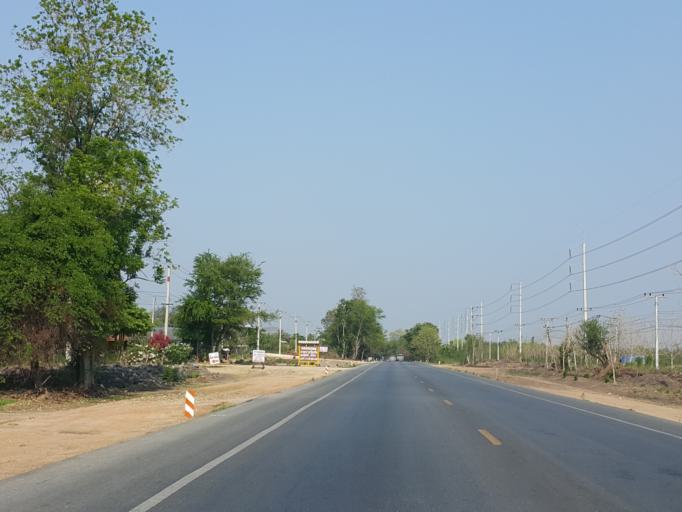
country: TH
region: Kanchanaburi
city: Sai Yok
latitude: 14.0895
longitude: 99.3177
